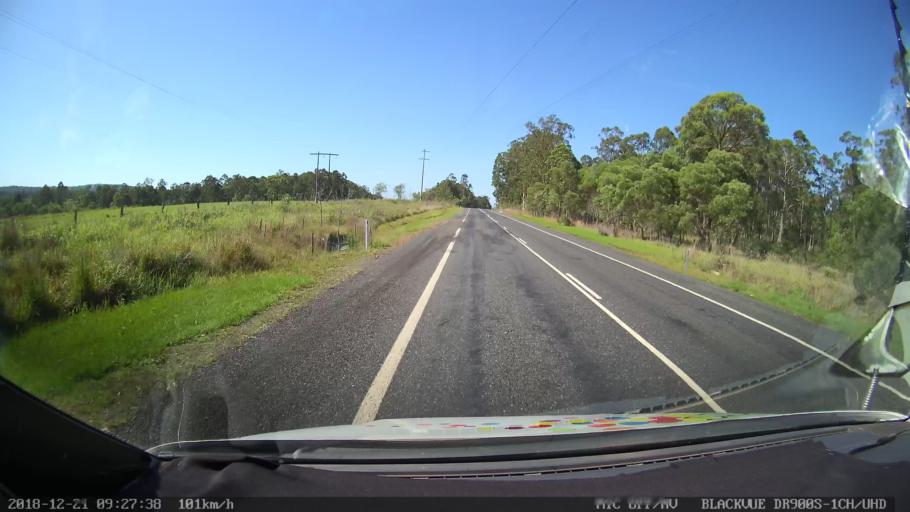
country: AU
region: New South Wales
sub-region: Clarence Valley
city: Maclean
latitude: -29.4057
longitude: 152.9892
